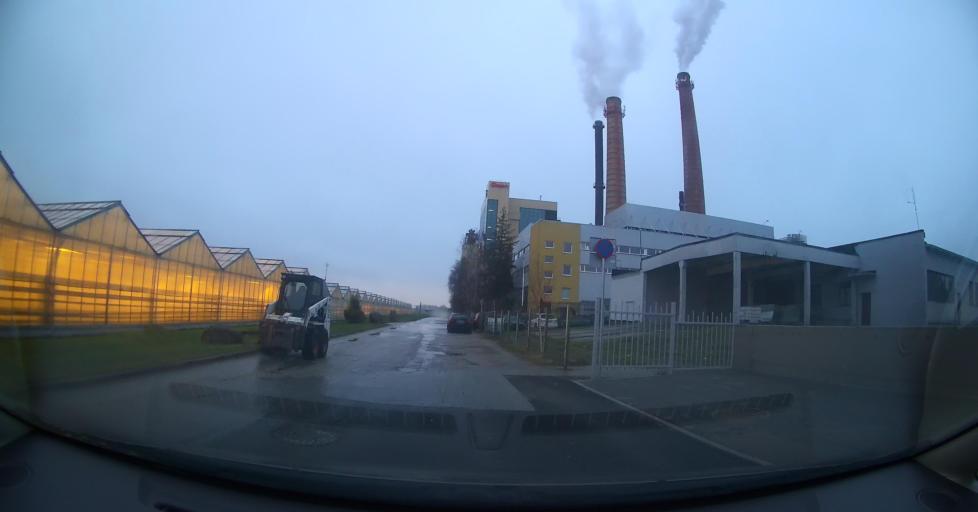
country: EE
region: Tartu
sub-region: Tartu linn
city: Tartu
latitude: 58.3693
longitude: 26.7935
